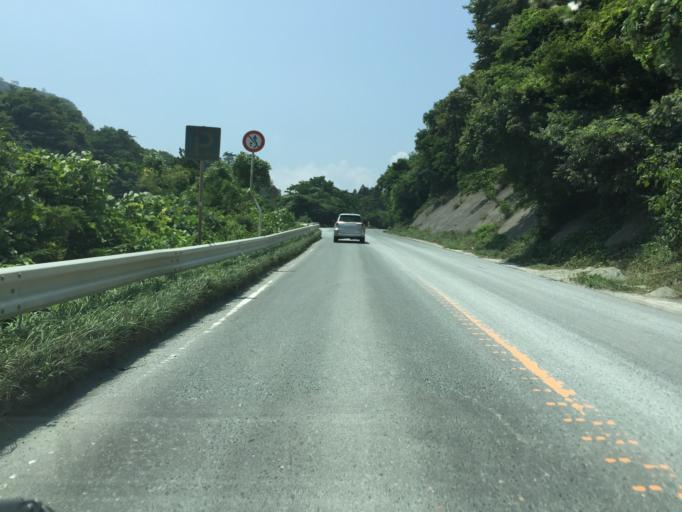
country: JP
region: Miyagi
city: Marumori
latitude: 37.8514
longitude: 140.8657
